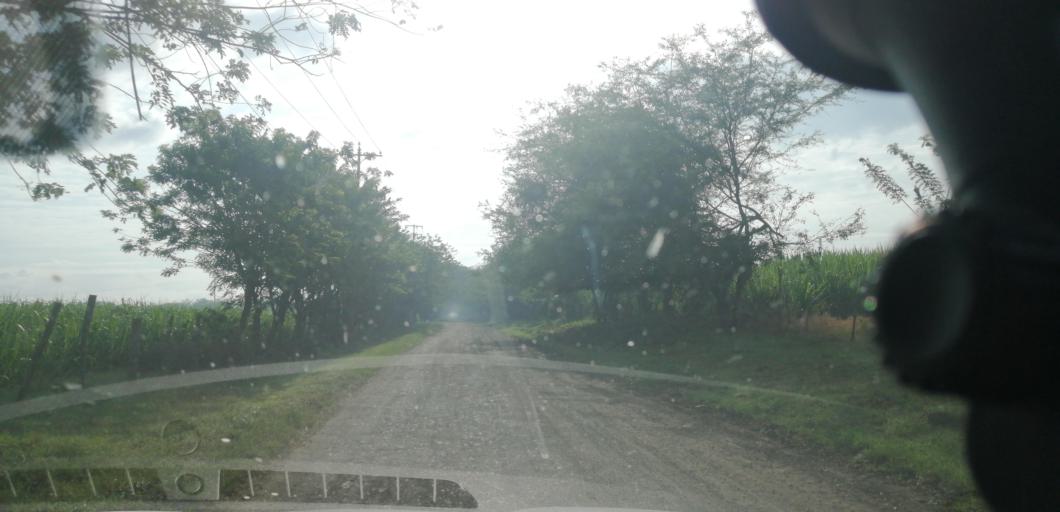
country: CO
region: Valle del Cauca
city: Yumbo
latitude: 3.5835
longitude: -76.4249
